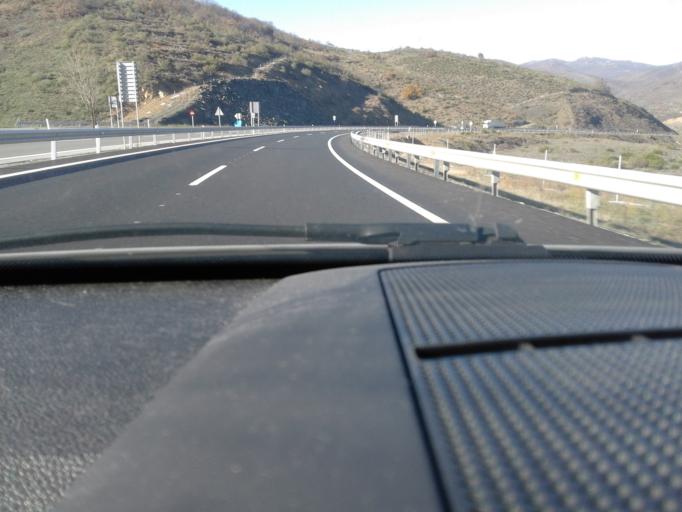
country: ES
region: Castille and Leon
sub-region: Provincia de Leon
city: Soto y Amio
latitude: 42.8173
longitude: -5.8521
